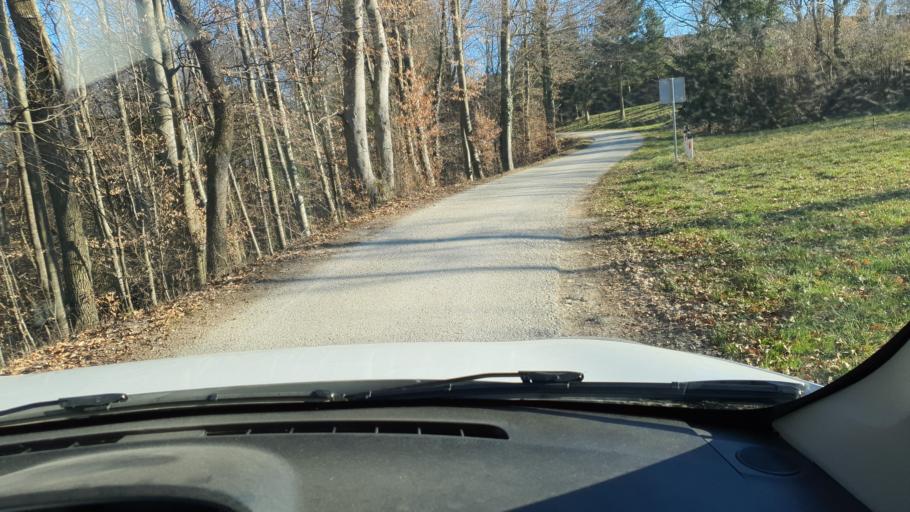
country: SI
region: Sveti Andraz v Slovenskih Goricah
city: Vitomarci
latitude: 46.5258
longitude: 15.9304
